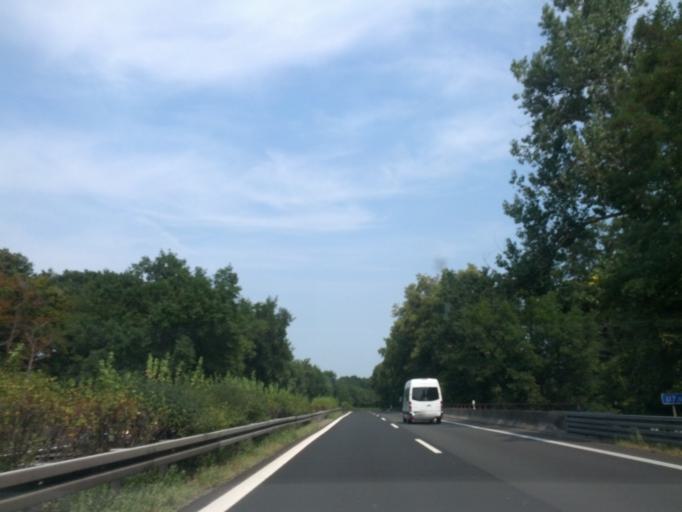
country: DE
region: Brandenburg
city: Werder
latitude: 52.4034
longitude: 12.8718
